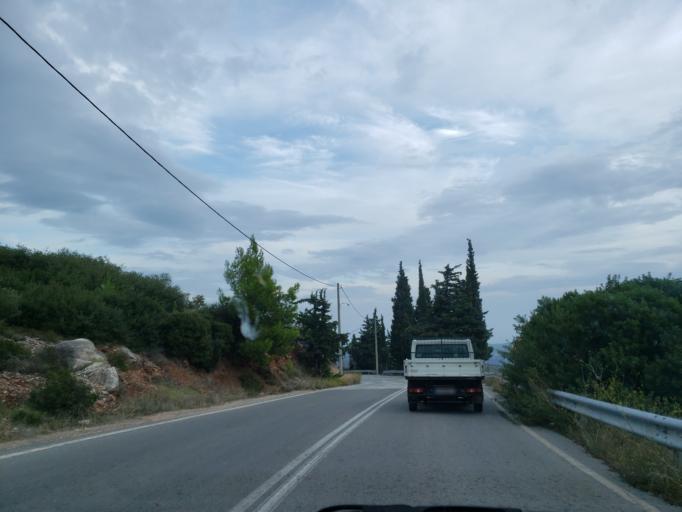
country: GR
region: Attica
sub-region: Nomarchia Anatolikis Attikis
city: Grammatiko
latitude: 38.2052
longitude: 23.9548
